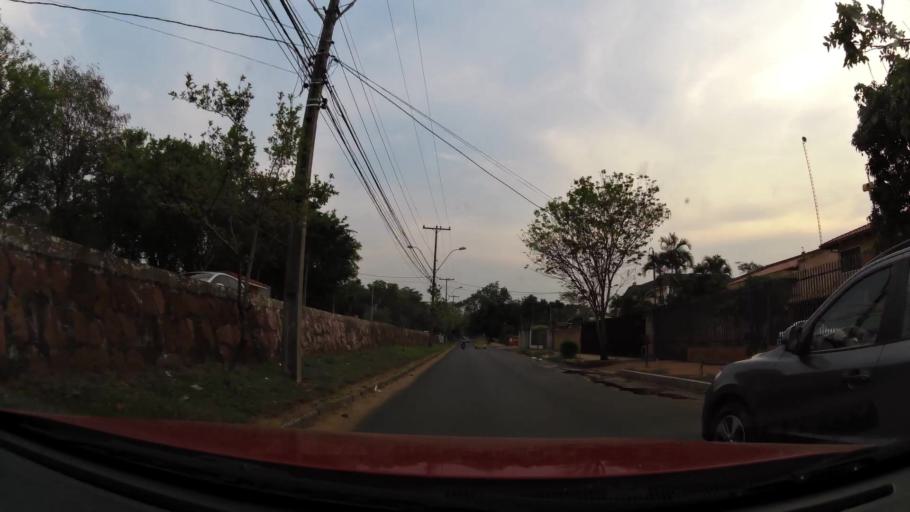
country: PY
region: Central
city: Lambare
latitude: -25.3449
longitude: -57.6387
